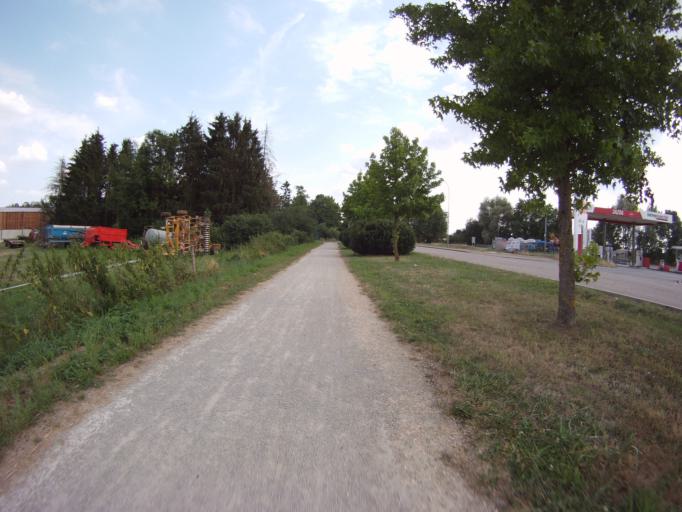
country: FR
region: Lorraine
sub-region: Departement de la Moselle
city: Courcelles-Chaussy
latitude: 49.1105
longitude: 6.3919
